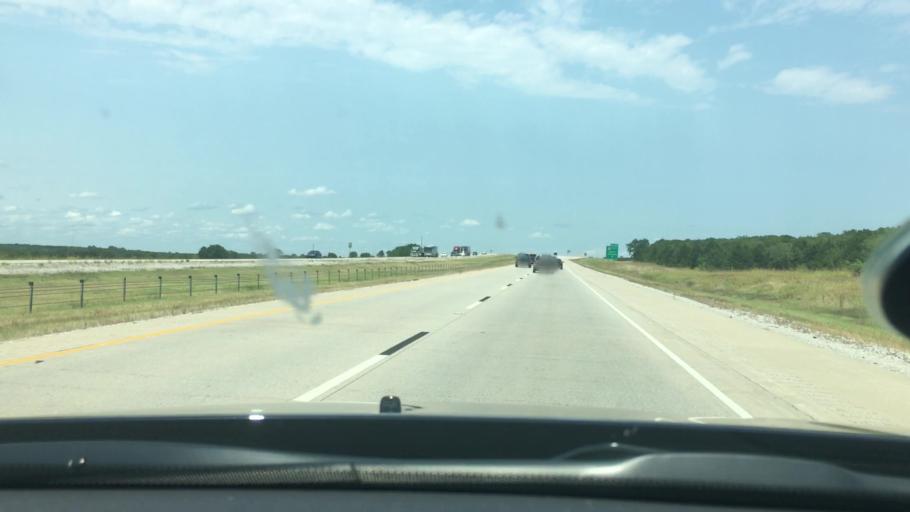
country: US
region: Oklahoma
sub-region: Carter County
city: Ardmore
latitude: 34.1309
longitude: -97.1562
